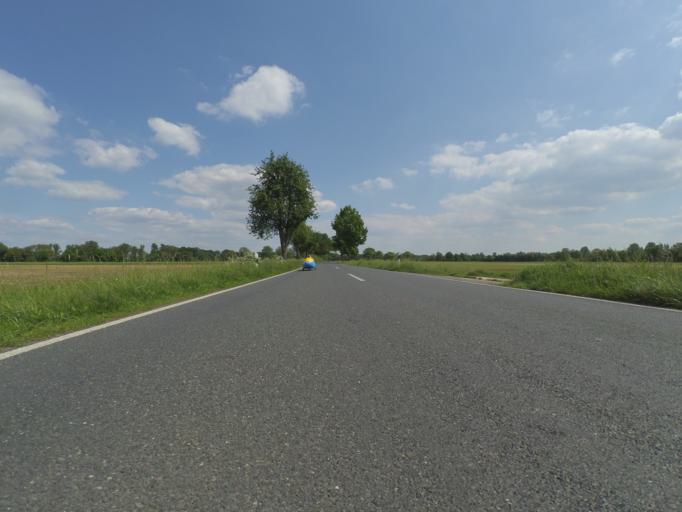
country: DE
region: Lower Saxony
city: Uetze
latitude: 52.4687
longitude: 10.2268
